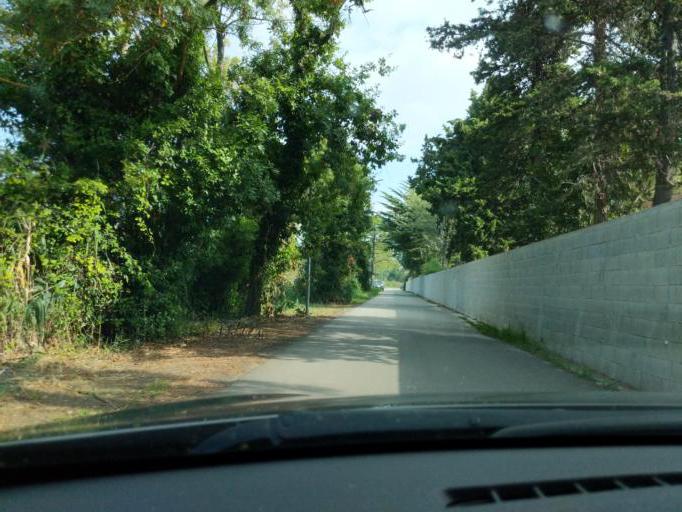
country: FR
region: Corsica
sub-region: Departement de la Haute-Corse
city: Ghisonaccia
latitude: 41.9972
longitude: 9.4413
